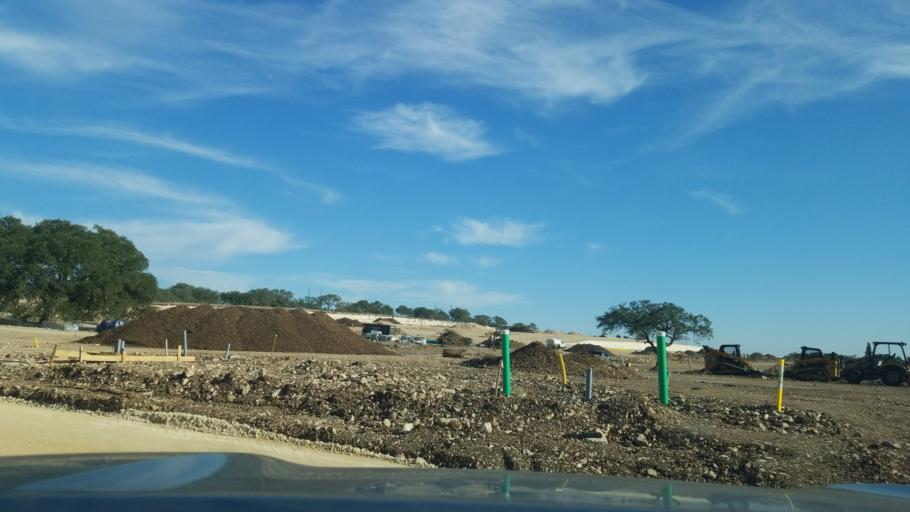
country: US
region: Texas
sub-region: Comal County
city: Canyon Lake
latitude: 29.7864
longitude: -98.2884
